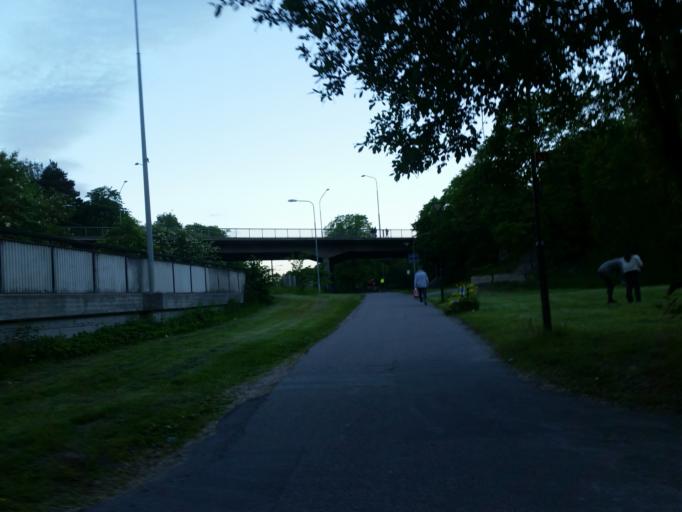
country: SE
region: Stockholm
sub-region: Stockholms Kommun
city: Arsta
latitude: 59.2990
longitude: 18.0754
